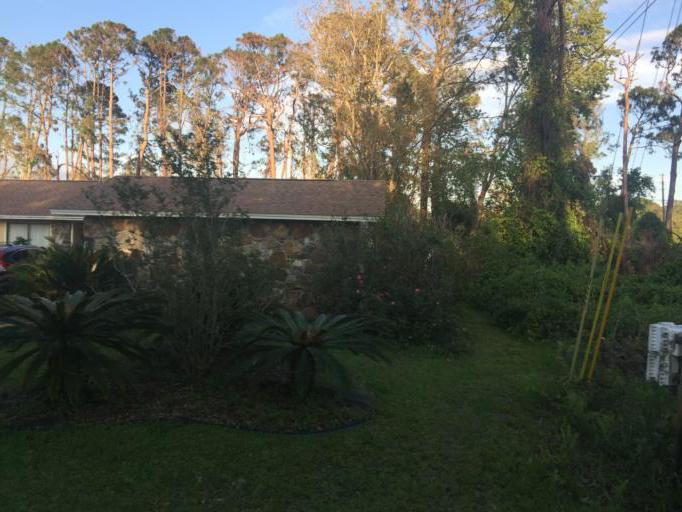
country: US
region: Florida
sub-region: Bay County
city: Panama City Beach
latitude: 30.2132
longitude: -85.8446
